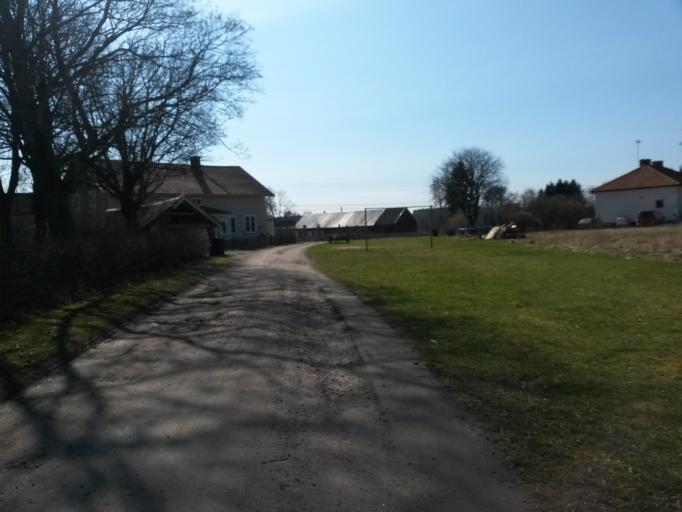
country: SE
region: Vaestra Goetaland
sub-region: Vargarda Kommun
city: Vargarda
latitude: 58.0321
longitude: 12.7890
